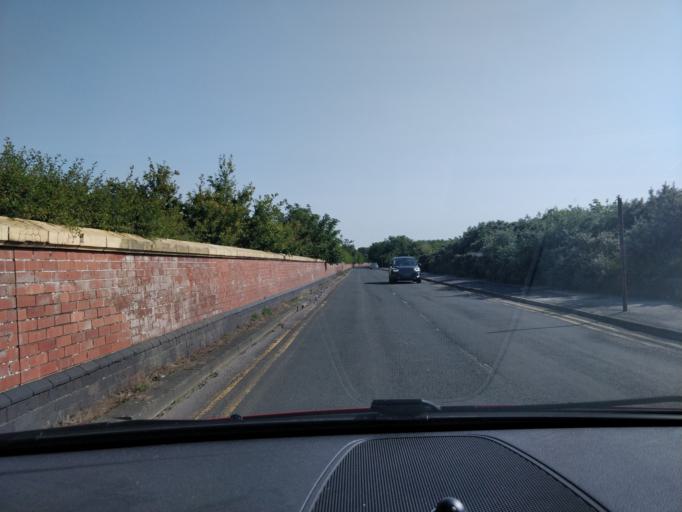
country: GB
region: England
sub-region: Sefton
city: Southport
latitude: 53.6449
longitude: -3.0223
